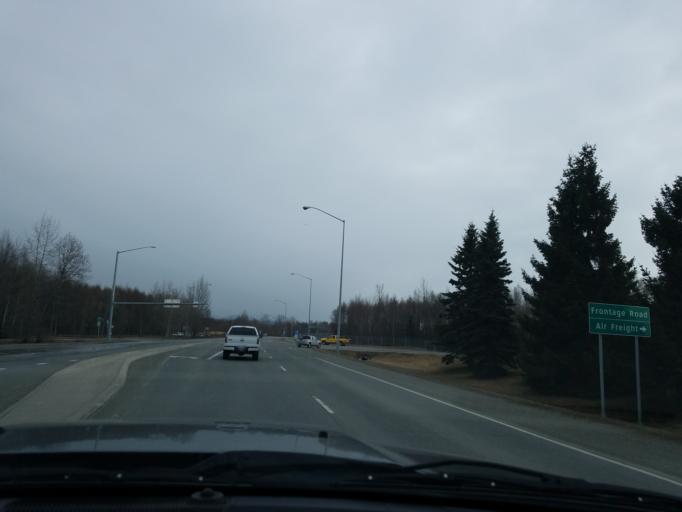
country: US
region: Alaska
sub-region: Anchorage Municipality
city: Anchorage
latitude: 61.1730
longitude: -149.9427
